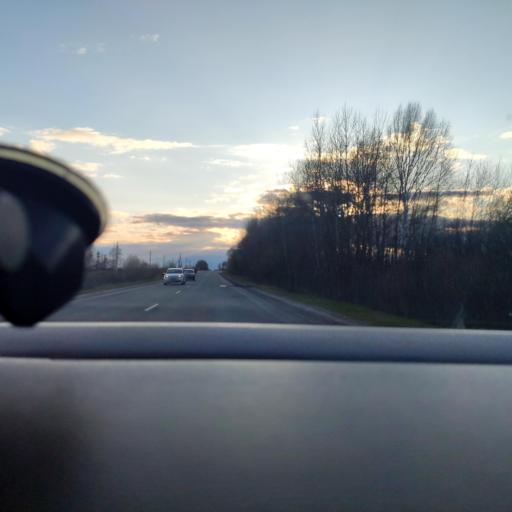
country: RU
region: Moskovskaya
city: Krasnyy Tkach
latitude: 55.4280
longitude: 39.2498
